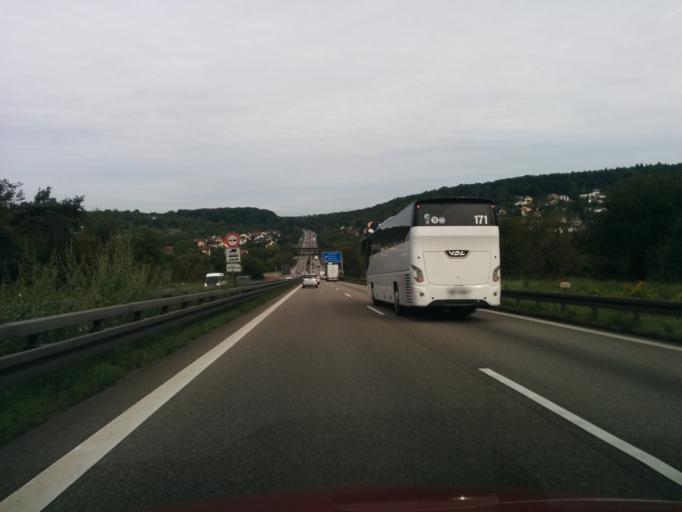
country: DE
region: Baden-Wuerttemberg
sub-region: Karlsruhe Region
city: Niefern-Oschelbronn
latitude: 48.9122
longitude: 8.7674
